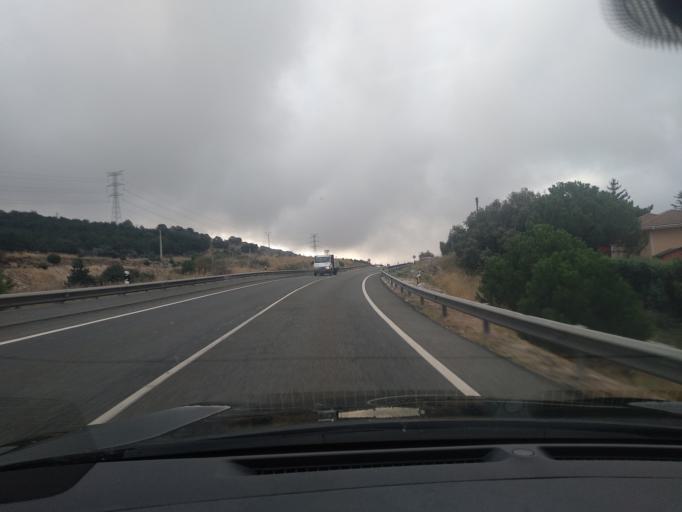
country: ES
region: Castille and Leon
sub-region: Provincia de Segovia
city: Otero de Herreros
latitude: 40.7823
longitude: -4.2111
